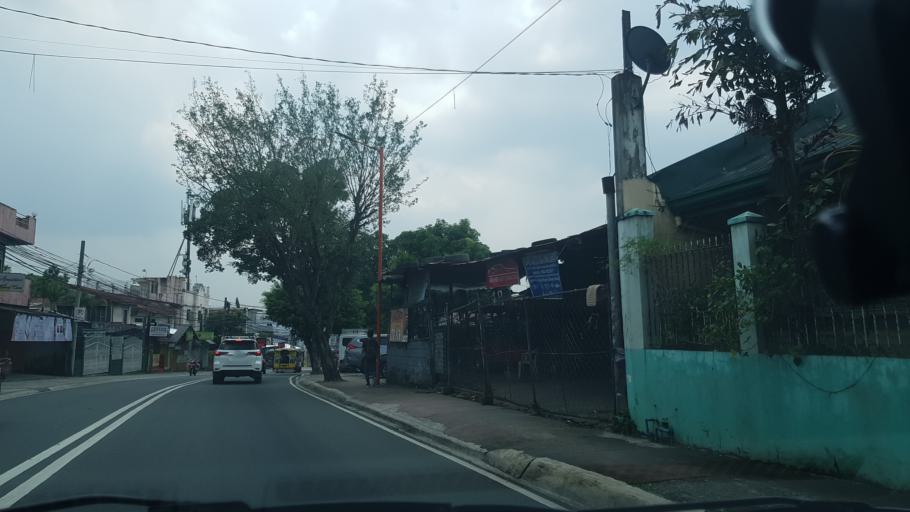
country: PH
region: Calabarzon
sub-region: Province of Rizal
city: Antipolo
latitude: 14.6439
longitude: 121.1213
